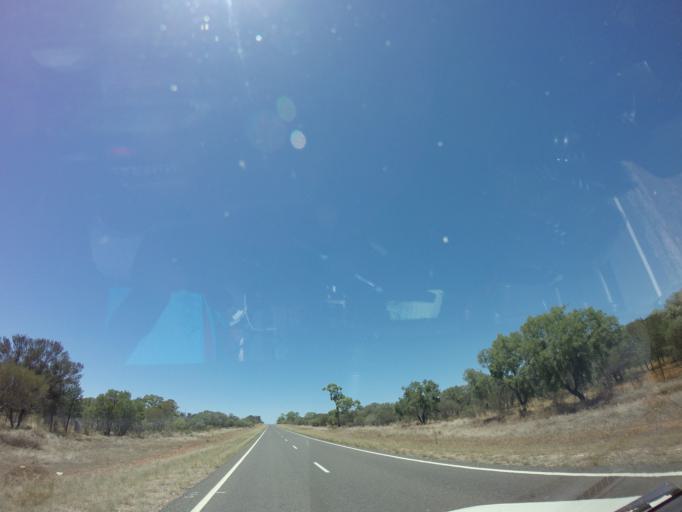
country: AU
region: New South Wales
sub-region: Cobar
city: Cobar
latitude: -31.5683
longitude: 144.7914
